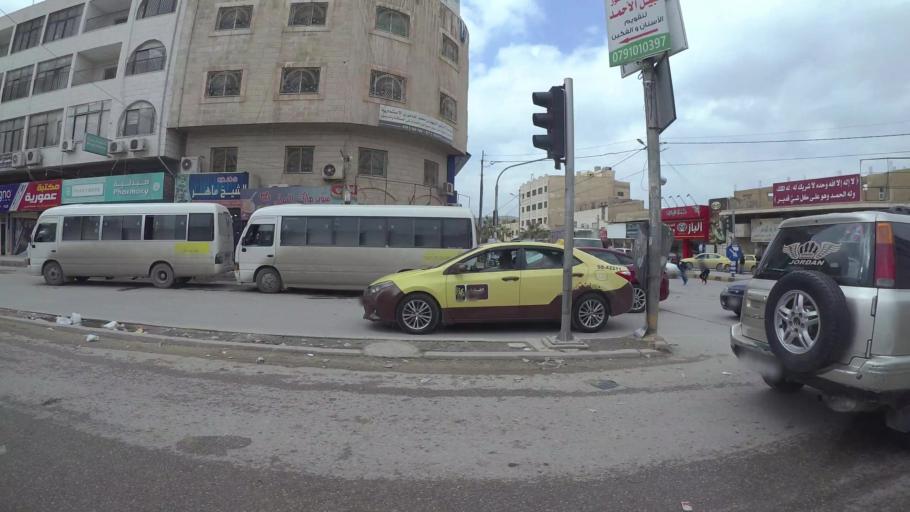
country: JO
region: Amman
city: Al Jubayhah
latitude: 32.0571
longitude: 35.8351
